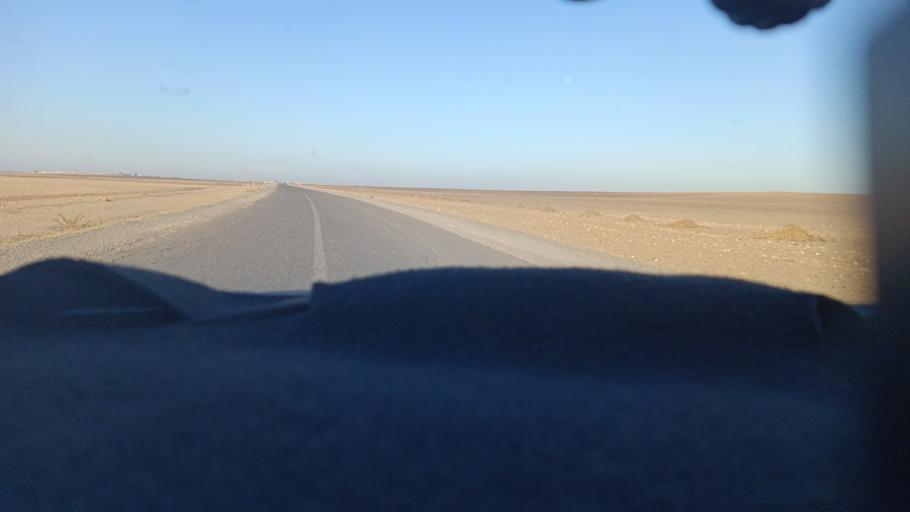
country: MA
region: Doukkala-Abda
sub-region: Safi
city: Youssoufia
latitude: 32.3695
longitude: -8.7332
